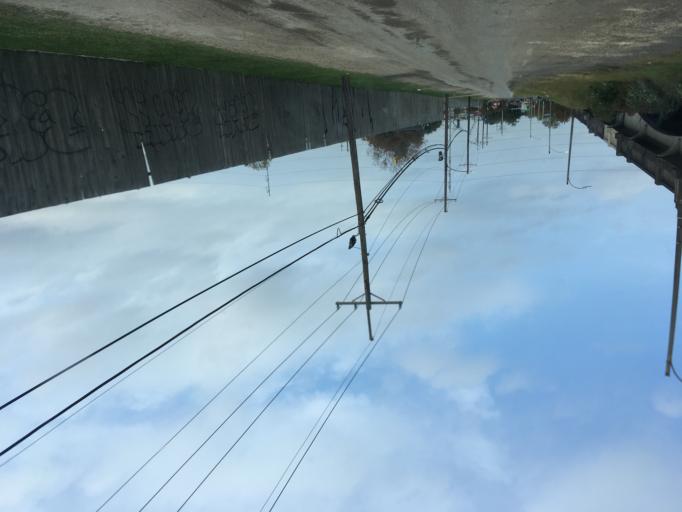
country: US
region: Louisiana
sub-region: Orleans Parish
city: New Orleans
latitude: 29.9870
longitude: -90.0581
